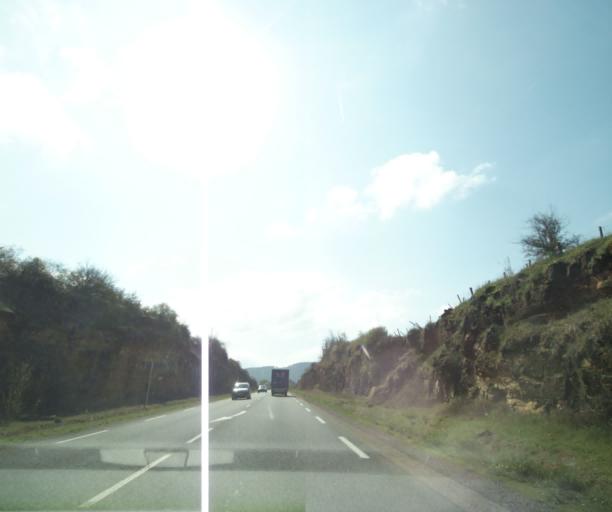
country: FR
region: Midi-Pyrenees
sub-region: Departement de l'Aveyron
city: Laissac
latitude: 44.3825
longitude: 2.8289
